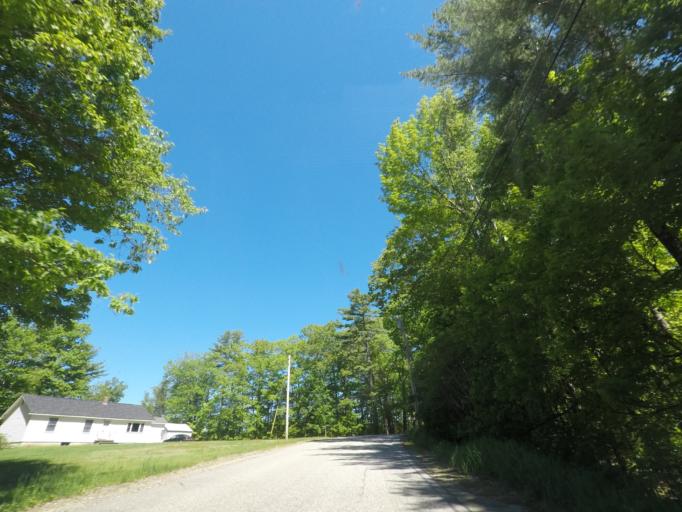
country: US
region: Maine
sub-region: Kennebec County
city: Winthrop
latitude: 44.2609
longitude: -69.9132
